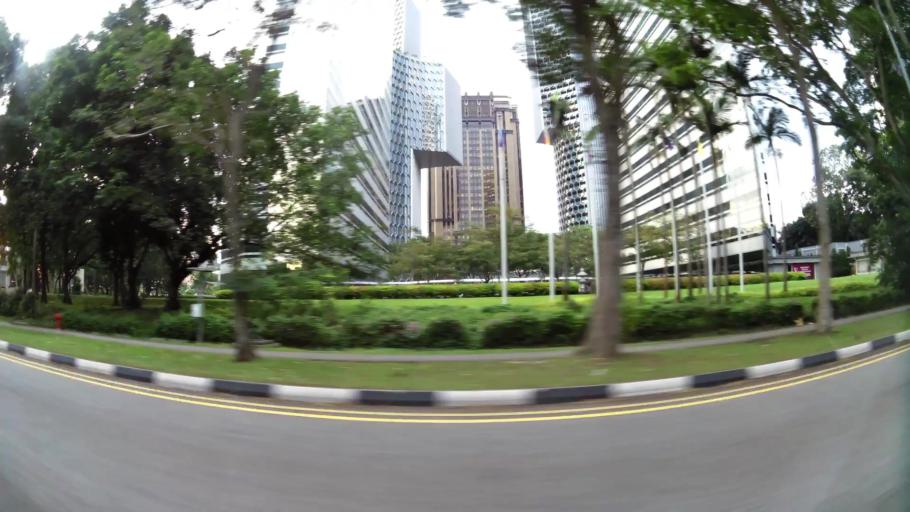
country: SG
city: Singapore
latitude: 1.2981
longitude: 103.8596
